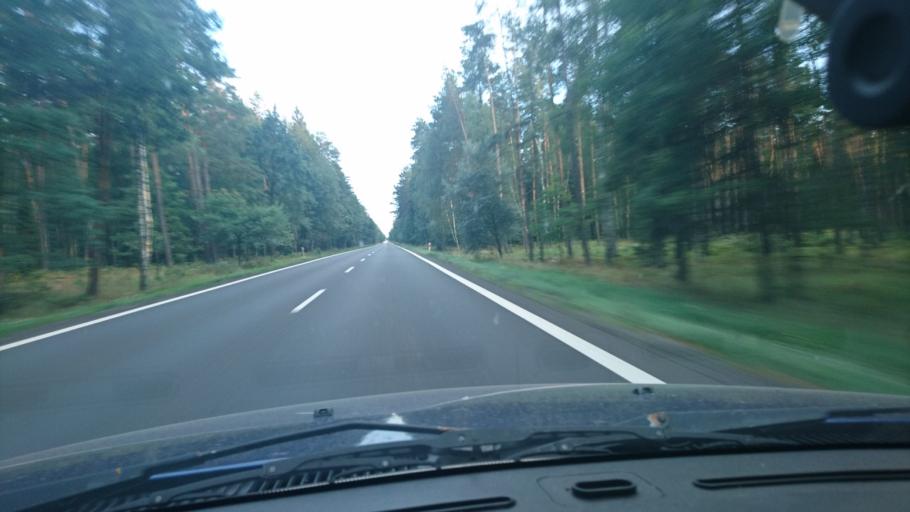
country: PL
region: Silesian Voivodeship
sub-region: Powiat tarnogorski
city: Tworog
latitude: 50.5769
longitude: 18.7090
